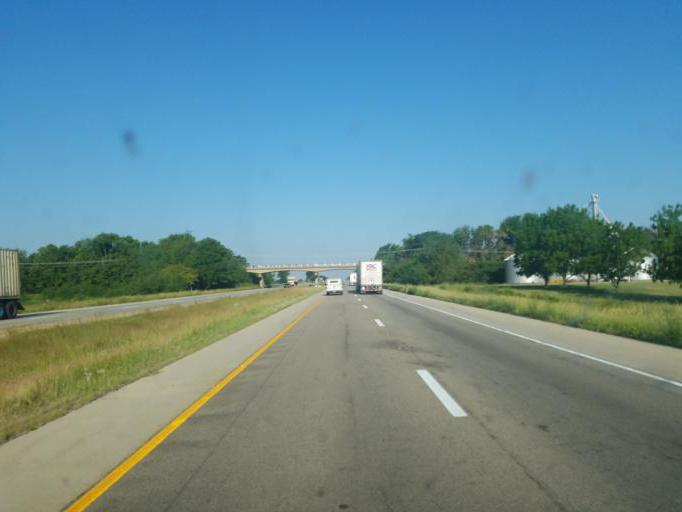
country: US
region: Illinois
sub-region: Grundy County
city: Morris
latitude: 41.3777
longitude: -88.5163
